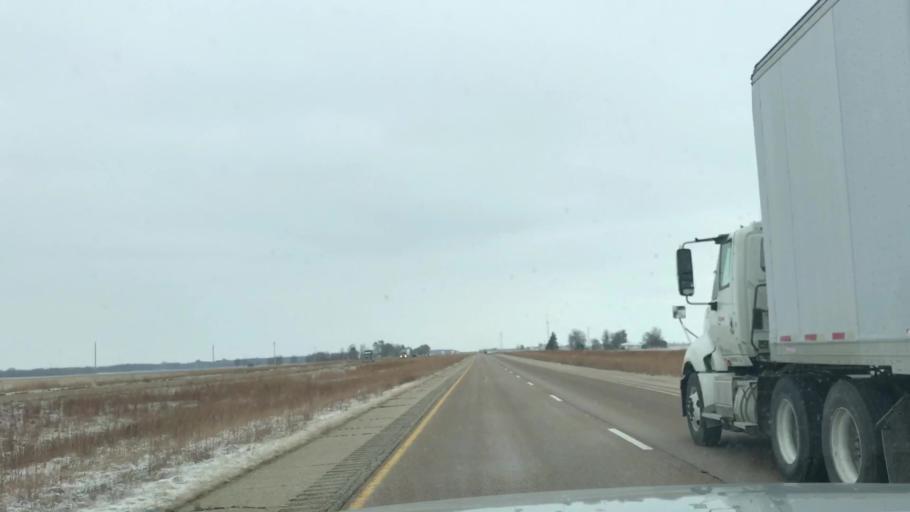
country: US
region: Illinois
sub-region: Montgomery County
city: Raymond
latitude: 39.4041
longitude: -89.6431
